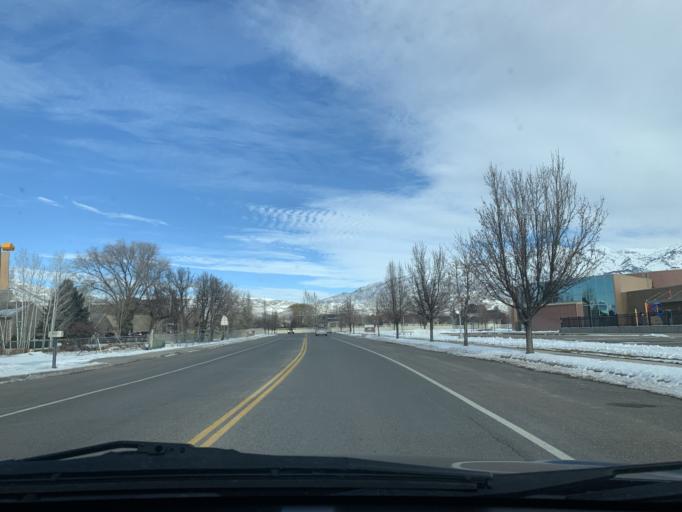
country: US
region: Utah
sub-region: Utah County
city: Lehi
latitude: 40.4193
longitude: -111.8211
